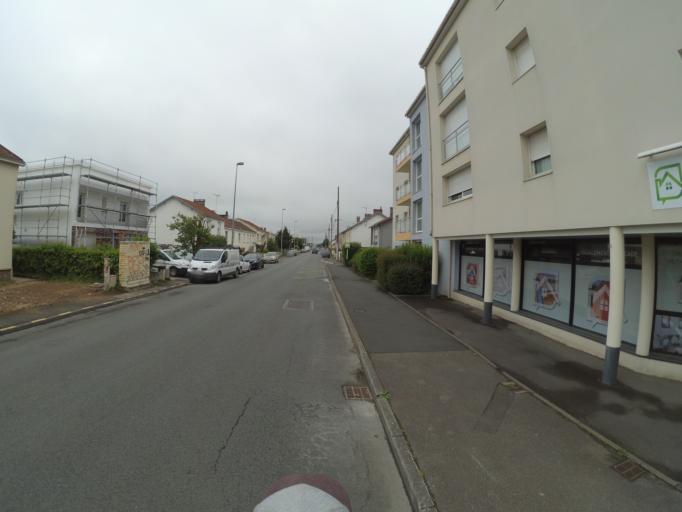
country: FR
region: Pays de la Loire
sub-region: Departement de la Vendee
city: La Roche-sur-Yon
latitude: 46.6556
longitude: -1.4324
